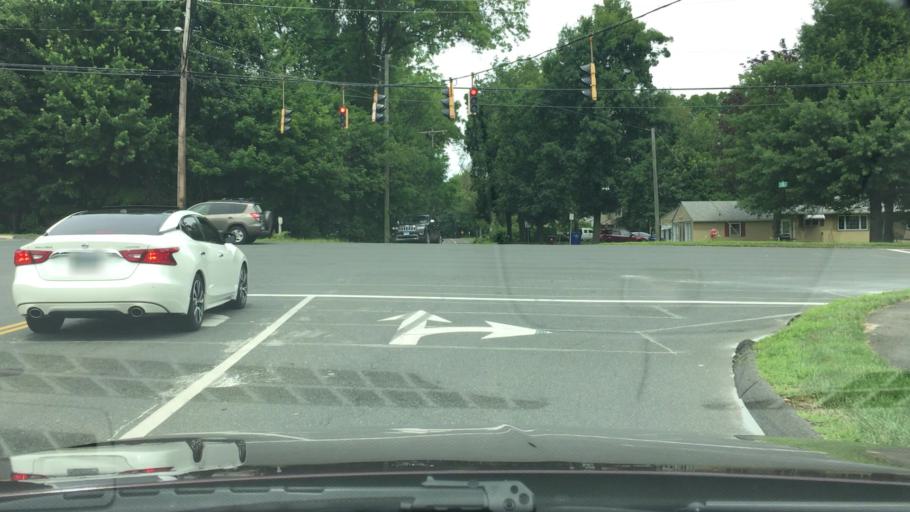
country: US
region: Connecticut
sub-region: Hartford County
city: Plainville
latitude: 41.7069
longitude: -72.8742
